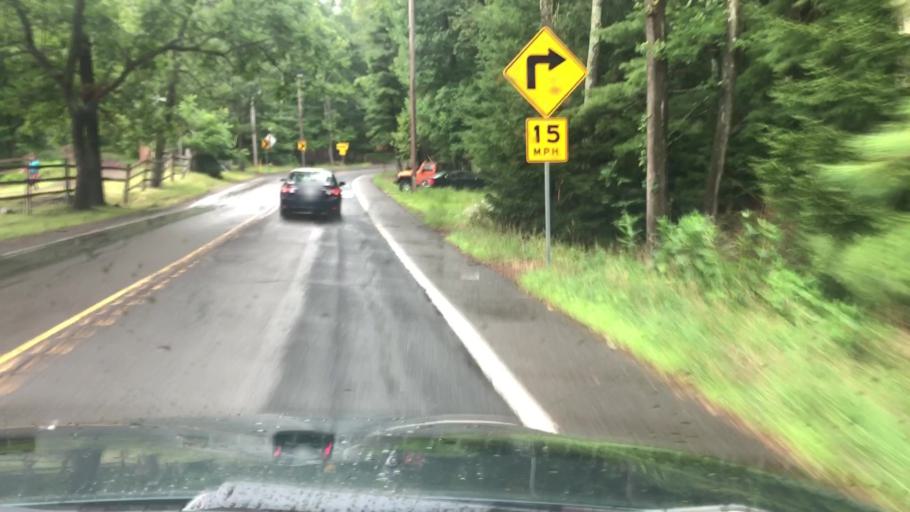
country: US
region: Pennsylvania
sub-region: Monroe County
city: Mountainhome
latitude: 41.2395
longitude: -75.2328
